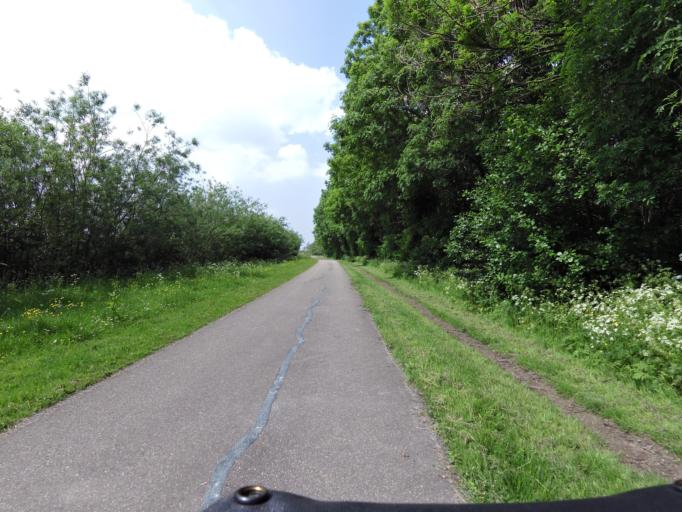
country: NL
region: South Holland
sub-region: Gemeente Spijkenisse
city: Spijkenisse
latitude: 51.8166
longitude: 4.2897
